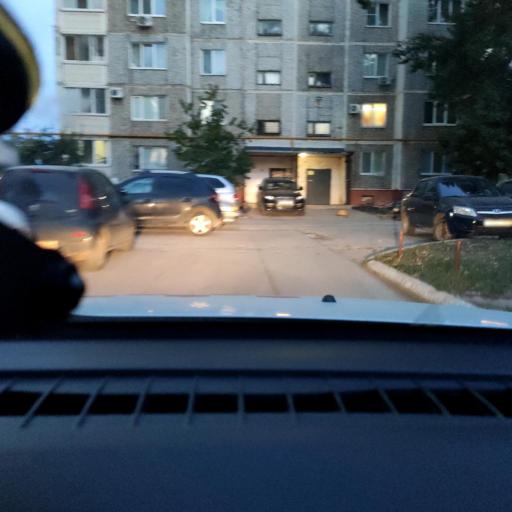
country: RU
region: Samara
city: Samara
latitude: 53.1057
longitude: 50.0824
